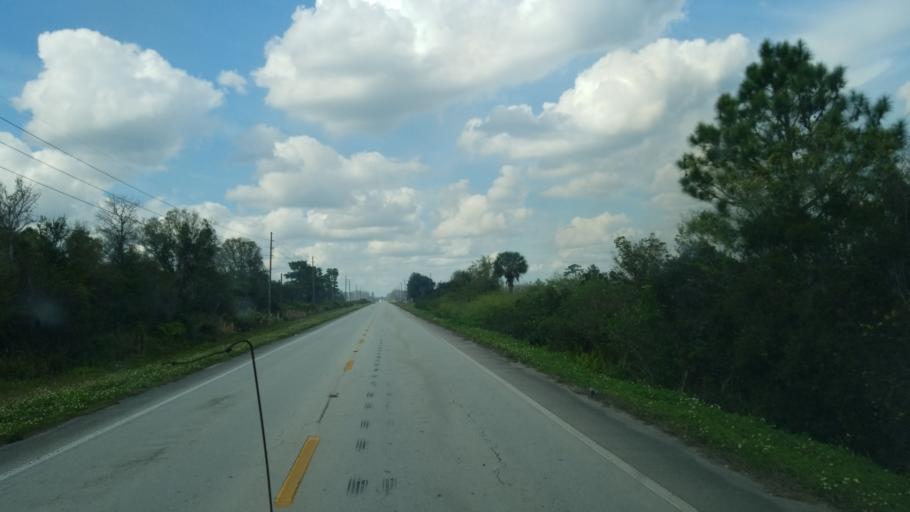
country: US
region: Florida
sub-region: Osceola County
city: Saint Cloud
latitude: 28.0535
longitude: -81.0554
